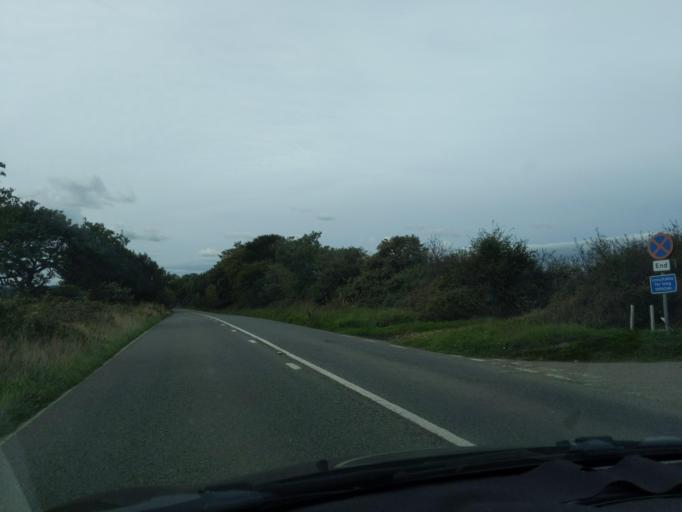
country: GB
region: England
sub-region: Cornwall
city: Lostwithiel
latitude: 50.4385
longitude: -4.6123
